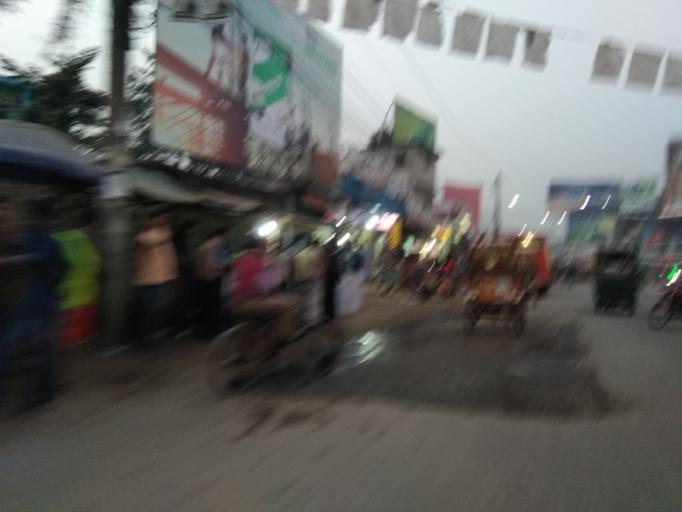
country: BD
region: Rangpur Division
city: Rangpur
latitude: 25.7400
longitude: 89.2544
